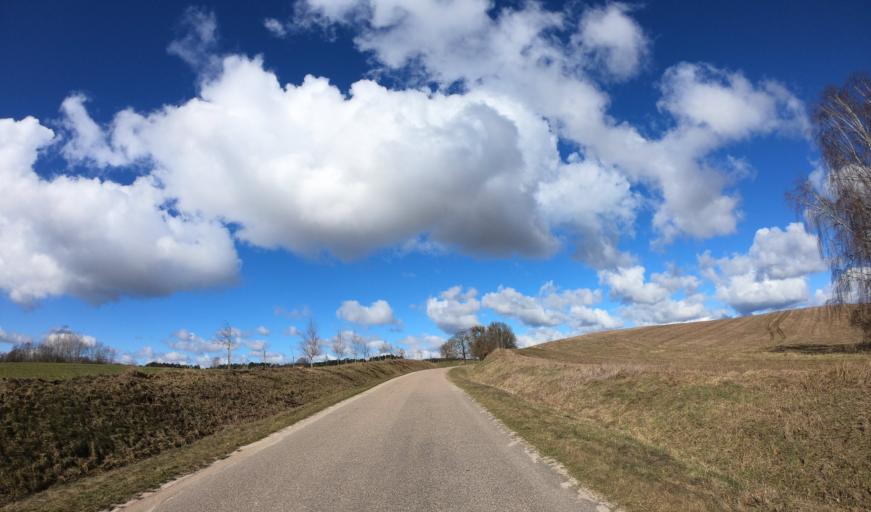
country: PL
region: West Pomeranian Voivodeship
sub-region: Powiat drawski
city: Zlocieniec
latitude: 53.4653
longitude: 15.9329
